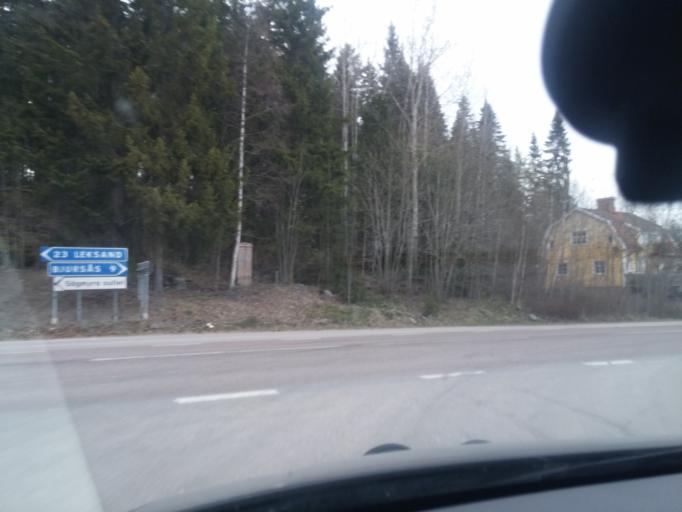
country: SE
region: Dalarna
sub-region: Faluns Kommun
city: Bjursas
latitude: 60.7110
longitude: 15.3123
